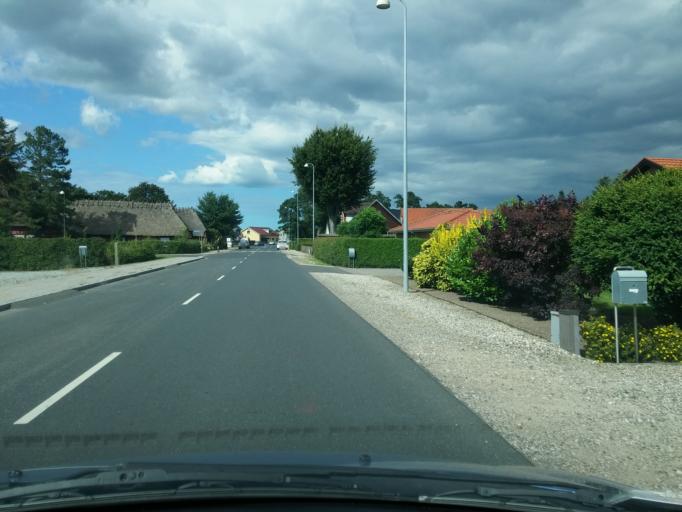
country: DK
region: South Denmark
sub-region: Odense Kommune
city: Bullerup
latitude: 55.4241
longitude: 10.4688
